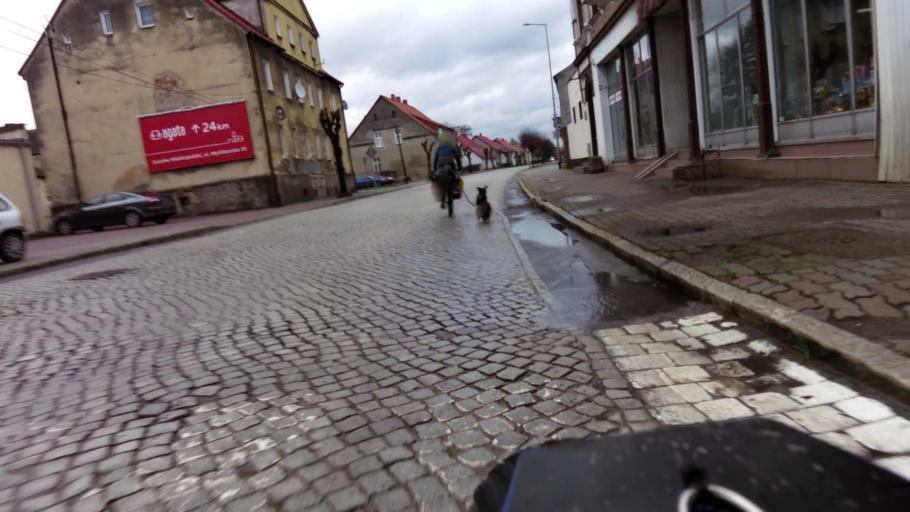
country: PL
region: Lubusz
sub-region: Powiat gorzowski
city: Witnica
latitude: 52.6735
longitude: 14.9007
